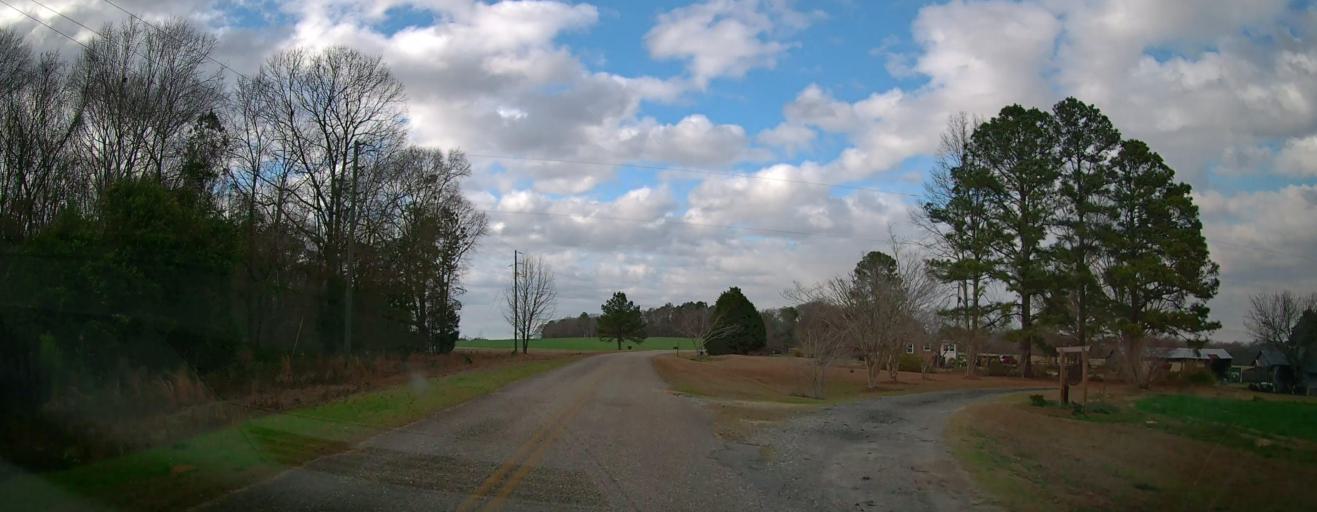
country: US
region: Georgia
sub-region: Marion County
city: Buena Vista
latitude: 32.4304
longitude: -84.4199
